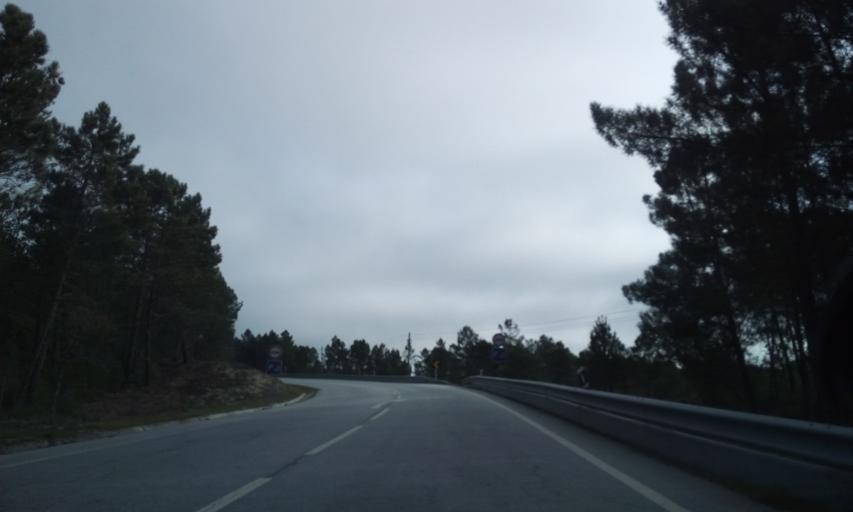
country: PT
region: Guarda
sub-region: Aguiar da Beira
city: Aguiar da Beira
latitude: 40.7808
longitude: -7.5045
